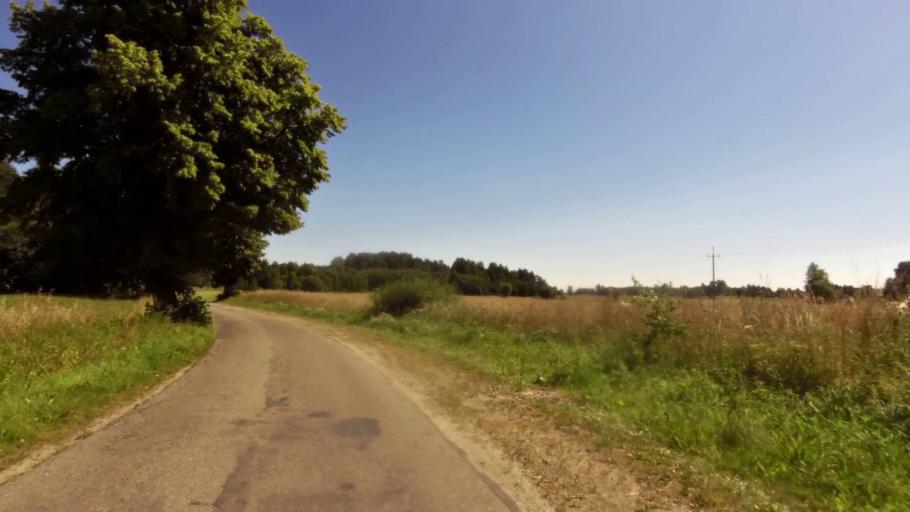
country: PL
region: West Pomeranian Voivodeship
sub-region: Powiat szczecinecki
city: Bialy Bor
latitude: 53.8907
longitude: 16.9056
